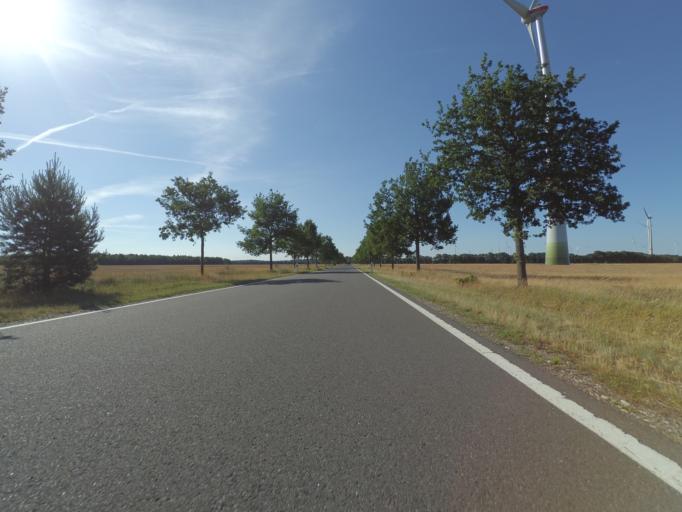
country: DE
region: Mecklenburg-Vorpommern
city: Siggelkow
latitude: 53.3537
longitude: 12.0334
